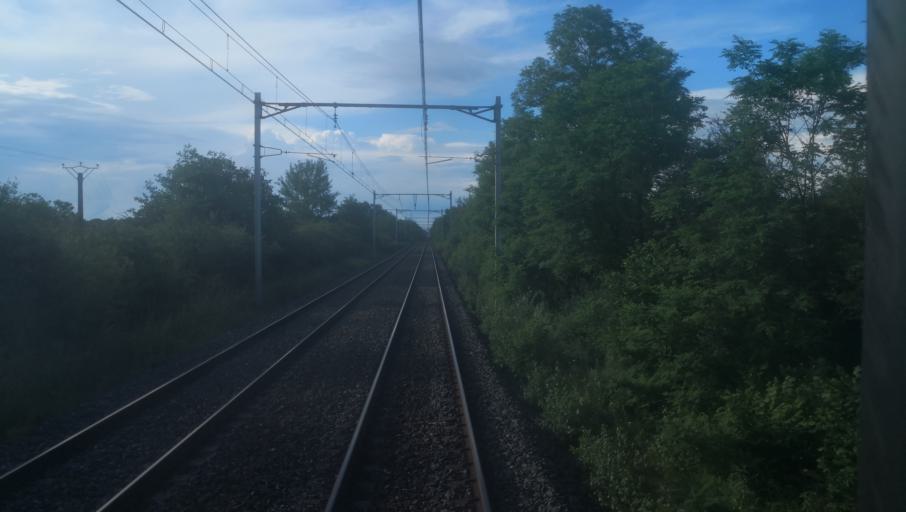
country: FR
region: Centre
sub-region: Departement du Loir-et-Cher
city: Theillay
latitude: 47.3000
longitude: 2.0430
